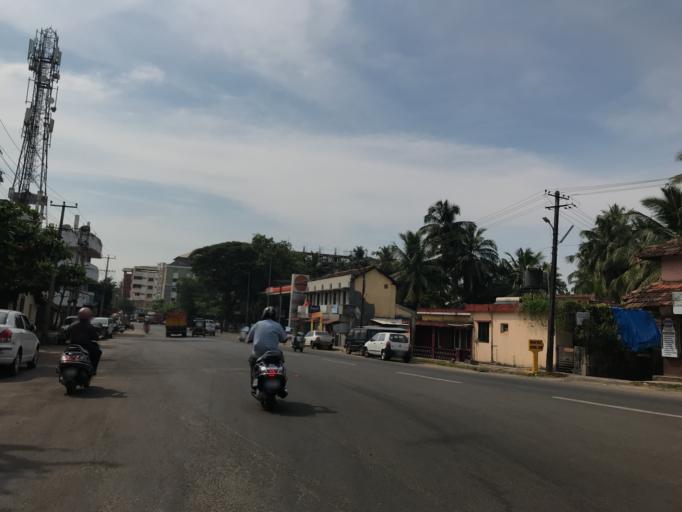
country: IN
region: Karnataka
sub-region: Dakshina Kannada
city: Ullal
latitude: 12.8499
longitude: 74.8493
